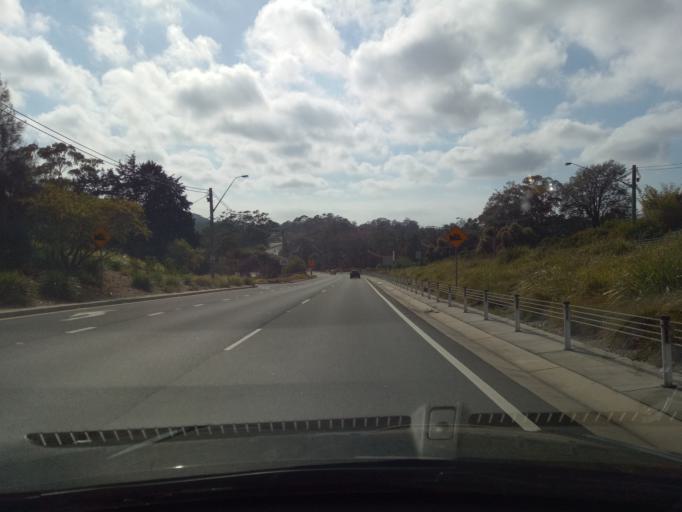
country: AU
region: New South Wales
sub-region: Gosford Shire
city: Holgate
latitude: -33.4258
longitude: 151.4229
